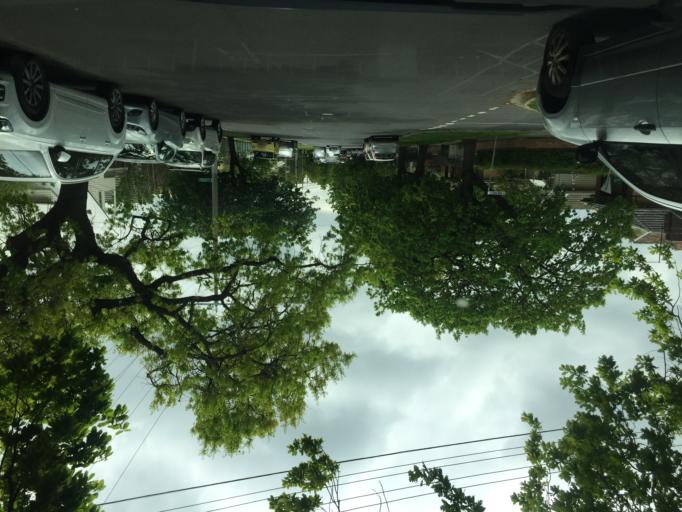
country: AU
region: Victoria
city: Spotswood
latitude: -37.8191
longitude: 144.8869
